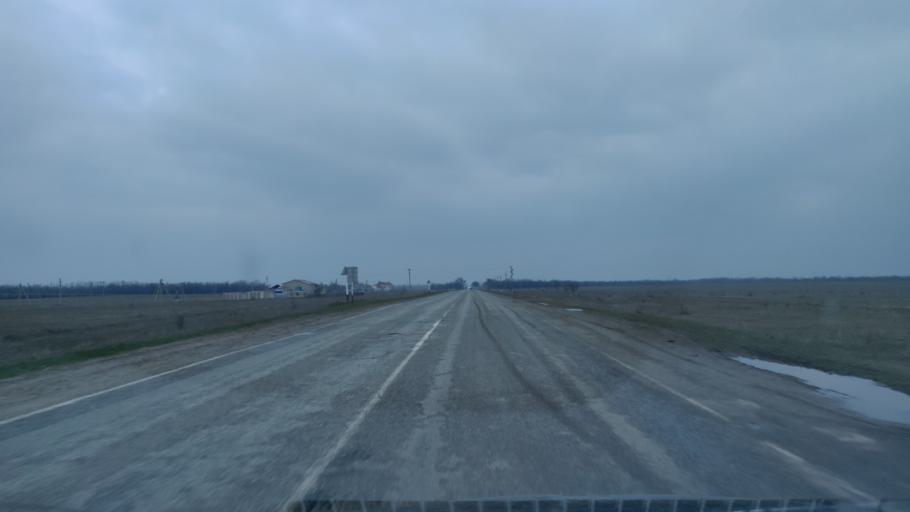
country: RU
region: Stavropol'skiy
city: Letnyaya Stavka
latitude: 45.3767
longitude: 43.3192
